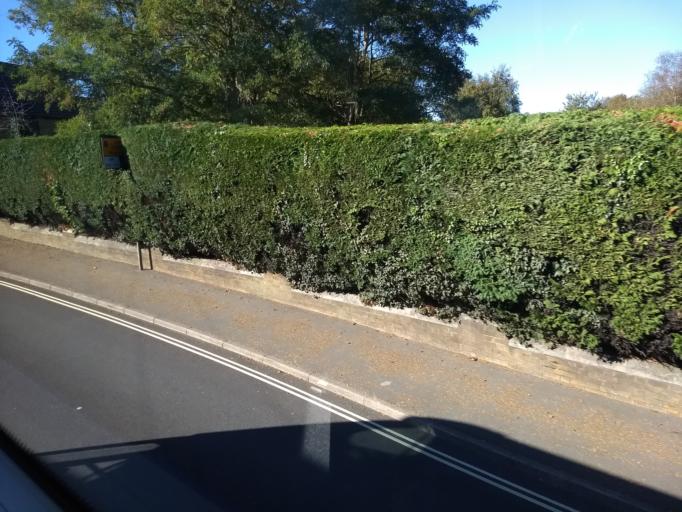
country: GB
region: England
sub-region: Isle of Wight
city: Newport
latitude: 50.7047
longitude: -1.2872
